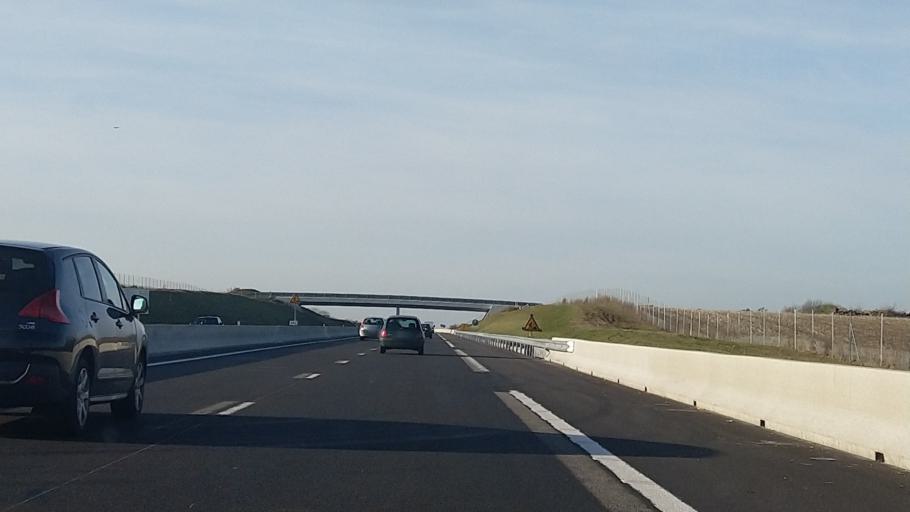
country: FR
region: Ile-de-France
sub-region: Departement du Val-d'Oise
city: Montsoult
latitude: 49.0842
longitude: 2.3217
